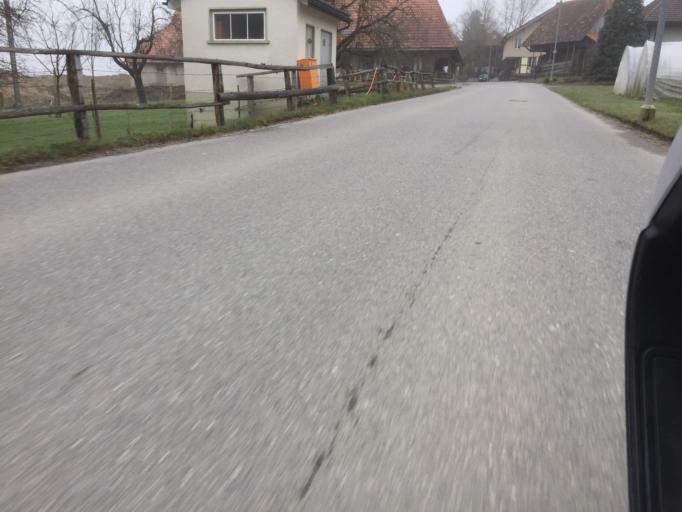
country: CH
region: Bern
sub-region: Seeland District
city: Grossaffoltern
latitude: 47.0864
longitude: 7.3775
